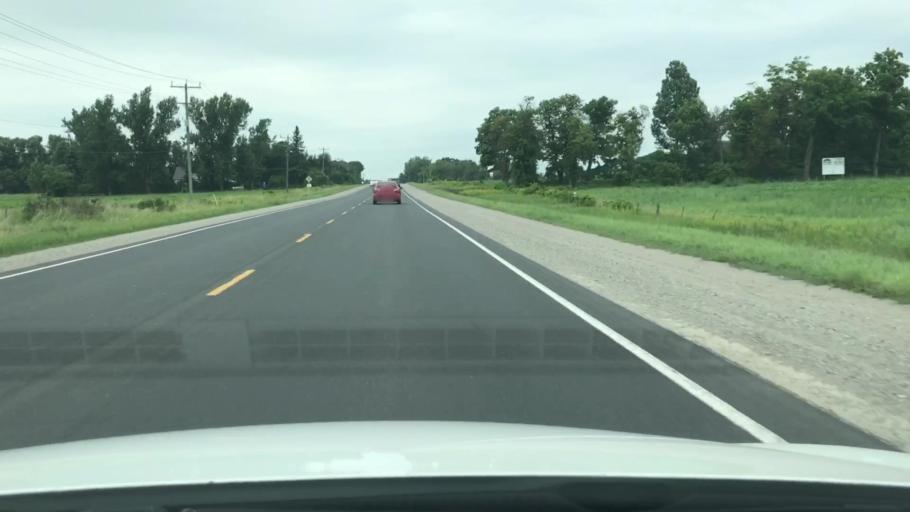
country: CA
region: Ontario
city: Bradford West Gwillimbury
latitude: 44.1773
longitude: -79.5802
